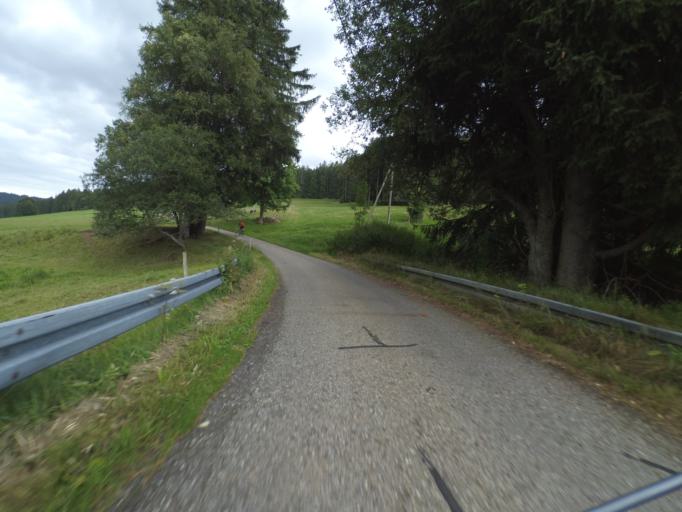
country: DE
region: Baden-Wuerttemberg
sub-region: Freiburg Region
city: Breitnau
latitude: 47.9556
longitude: 8.1349
